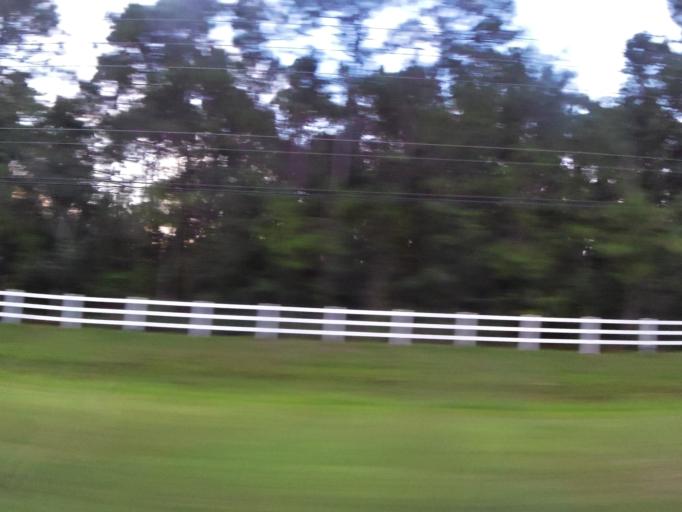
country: US
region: Florida
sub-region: Saint Johns County
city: Fruit Cove
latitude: 30.1176
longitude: -81.6054
